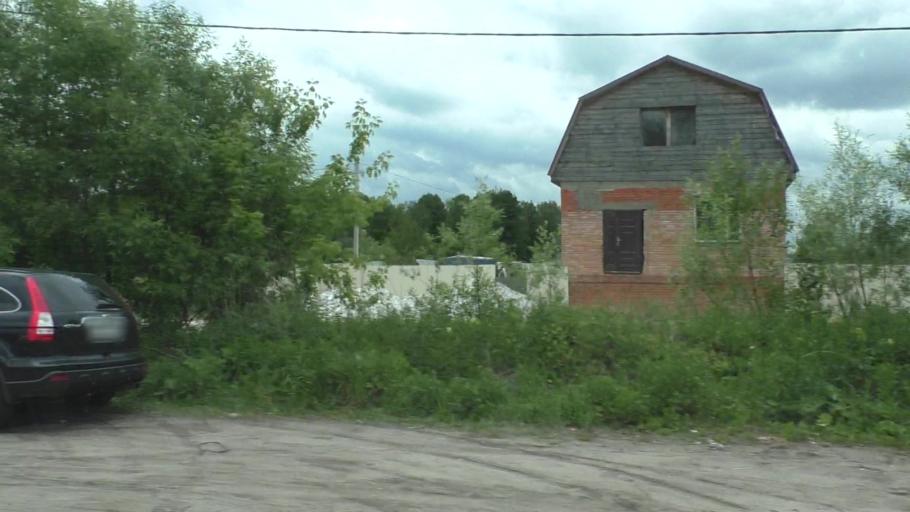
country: RU
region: Moskovskaya
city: Yegor'yevsk
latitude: 55.4009
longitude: 39.0052
